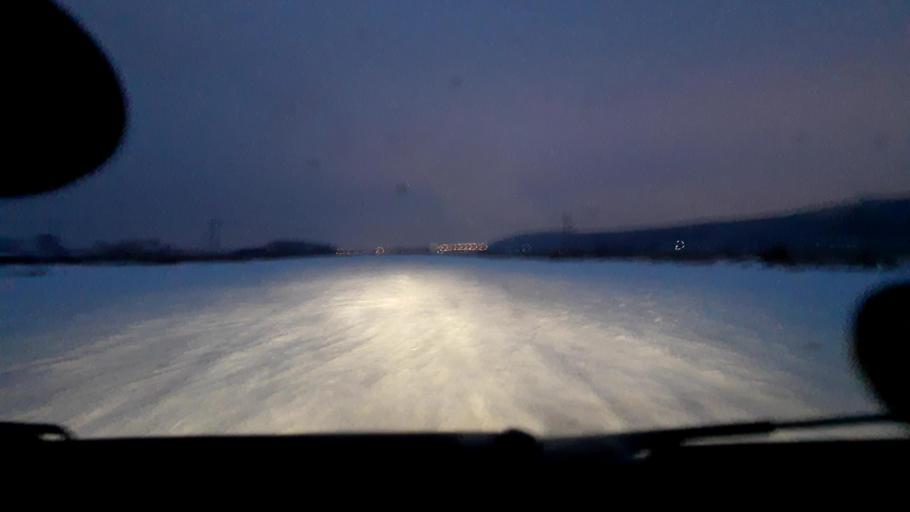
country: RU
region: Bashkortostan
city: Ufa
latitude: 54.8297
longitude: 56.1666
